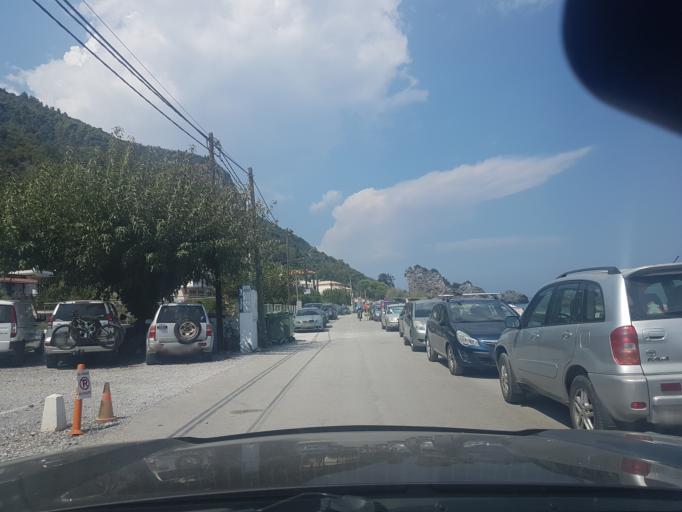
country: GR
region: Central Greece
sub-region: Nomos Evvoias
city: Kymi
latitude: 38.6698
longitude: 23.9224
